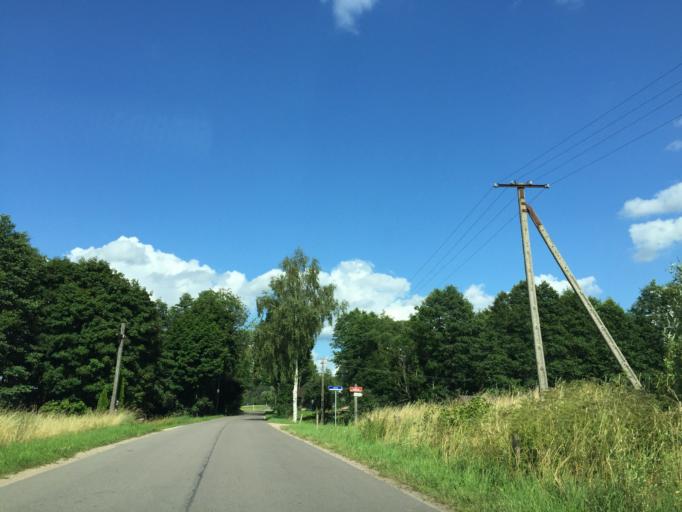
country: PL
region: Podlasie
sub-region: Suwalki
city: Suwalki
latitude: 54.1450
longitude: 23.0556
